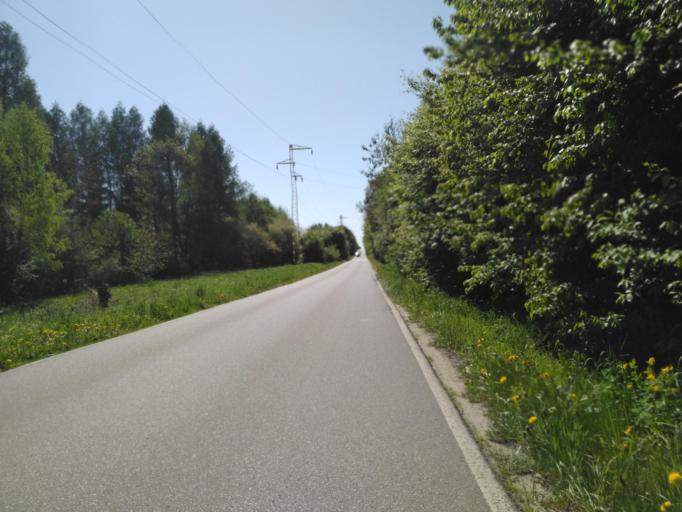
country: PL
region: Subcarpathian Voivodeship
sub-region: Krosno
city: Krosno
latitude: 49.6773
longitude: 21.7840
